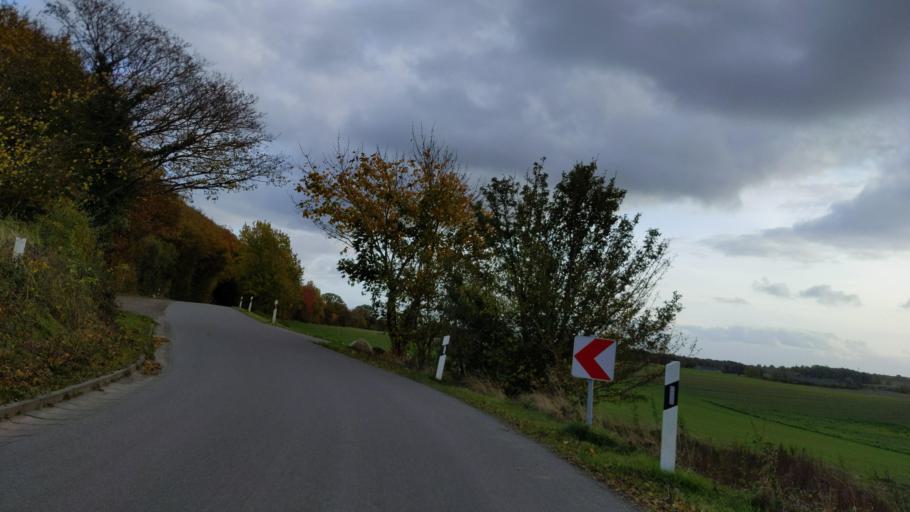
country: DE
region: Schleswig-Holstein
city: Kasseedorf
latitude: 54.1269
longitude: 10.7054
